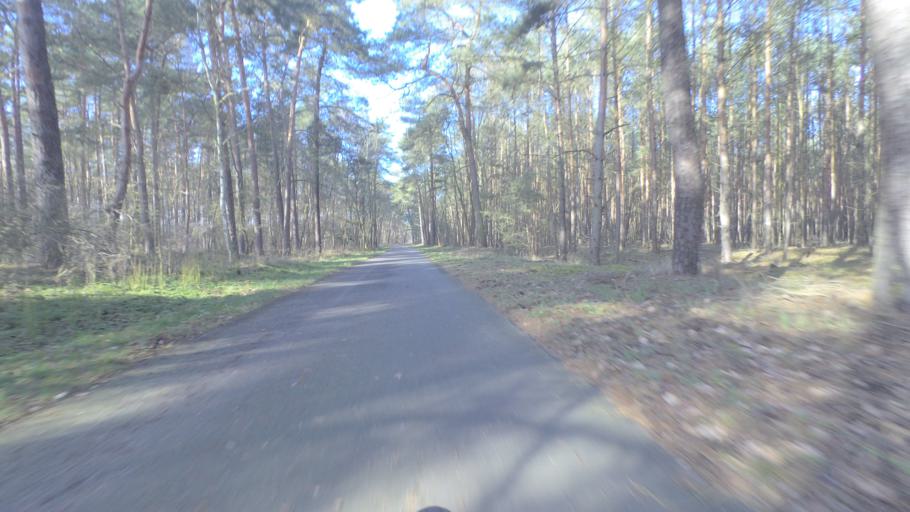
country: DE
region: Brandenburg
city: Luckenwalde
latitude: 52.0470
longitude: 13.1393
